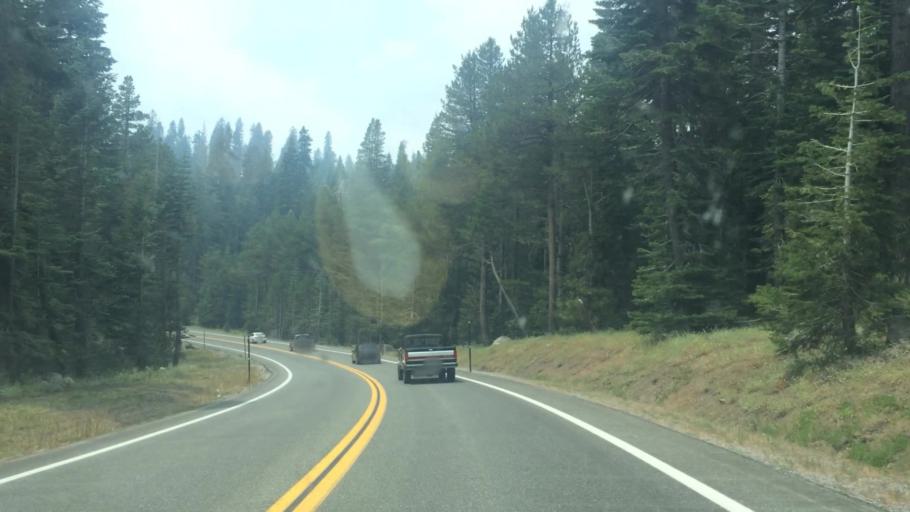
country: US
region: California
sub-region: Calaveras County
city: Arnold
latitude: 38.5959
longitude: -120.2276
